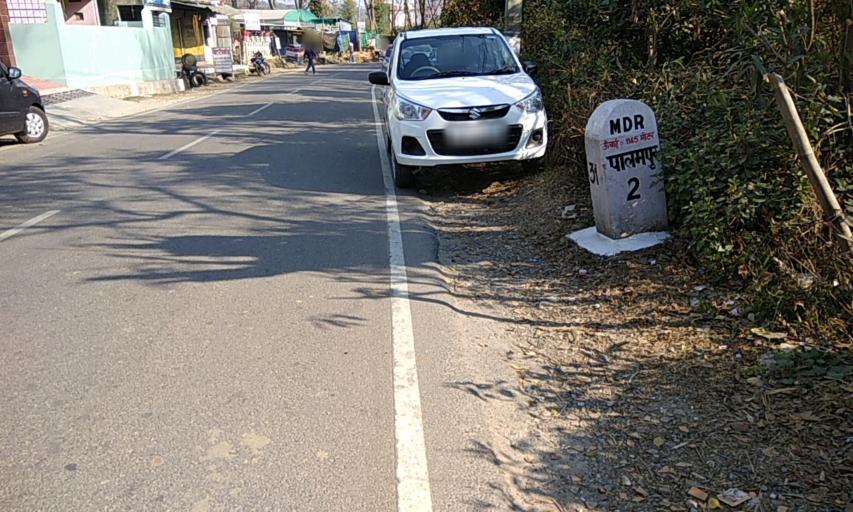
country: IN
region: Himachal Pradesh
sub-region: Kangra
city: Palampur
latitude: 32.1135
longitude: 76.5237
